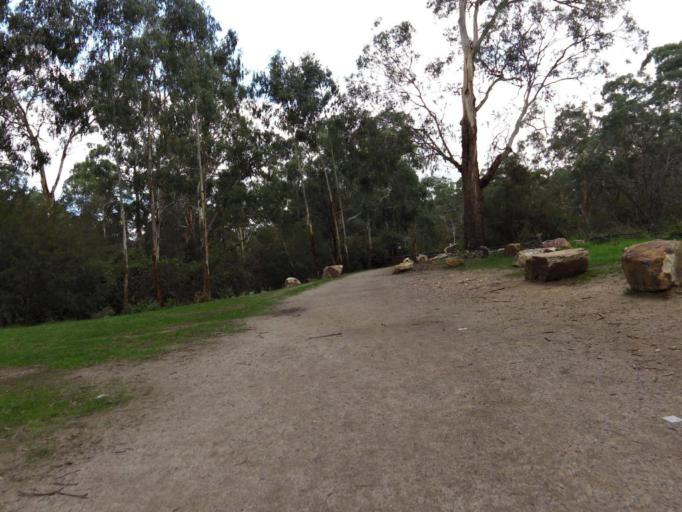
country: AU
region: Victoria
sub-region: Nillumbik
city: North Warrandyte
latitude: -37.7414
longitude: 145.2086
